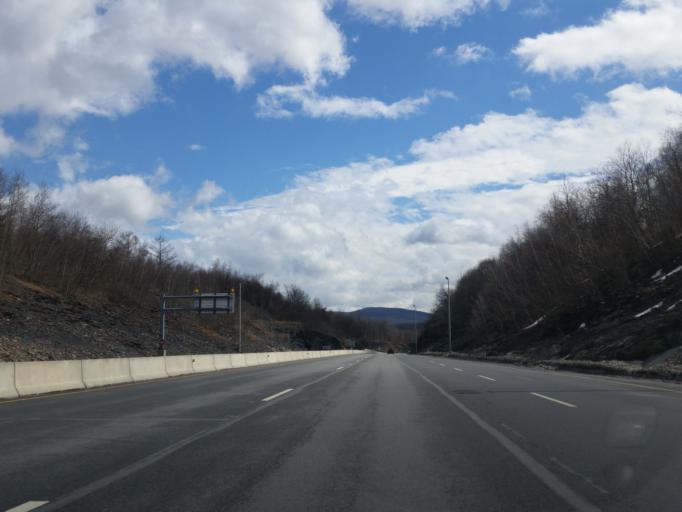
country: US
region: Pennsylvania
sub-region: Lackawanna County
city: Old Forge
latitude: 41.3825
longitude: -75.7262
